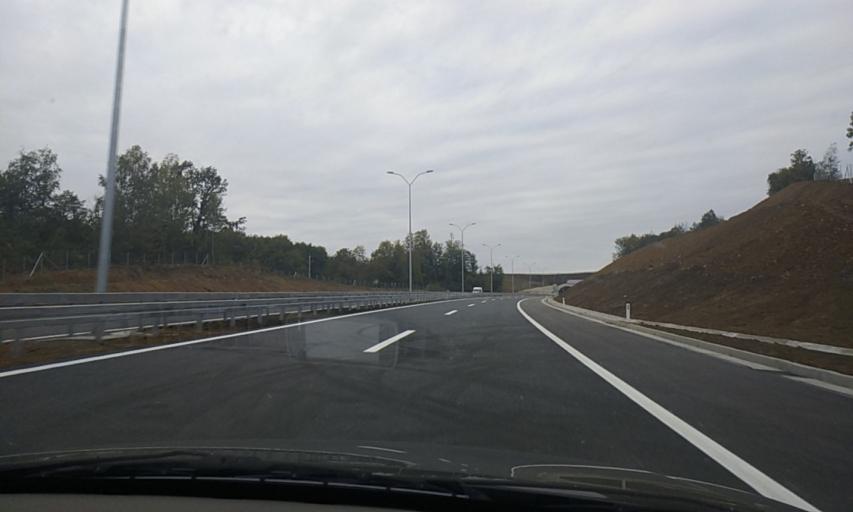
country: BA
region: Republika Srpska
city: Prnjavor
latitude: 44.8676
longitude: 17.5175
